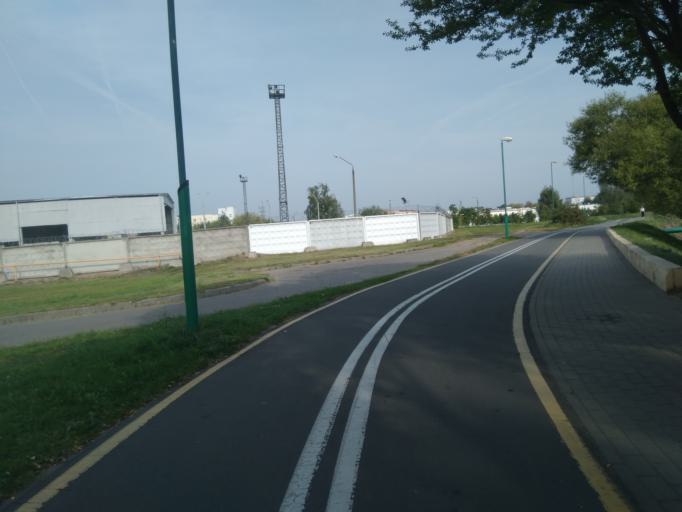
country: BY
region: Minsk
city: Minsk
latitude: 53.8770
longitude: 27.5791
